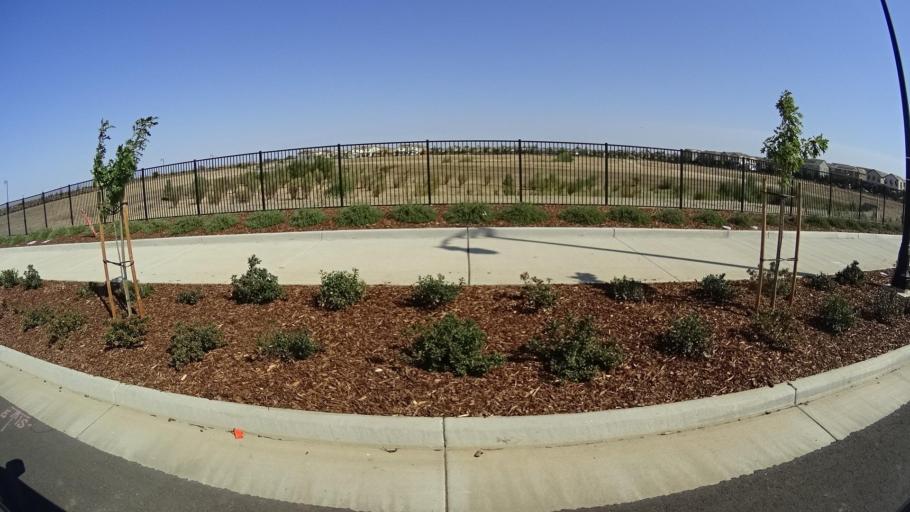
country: US
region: California
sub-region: Sacramento County
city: Elk Grove
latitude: 38.3801
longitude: -121.3792
